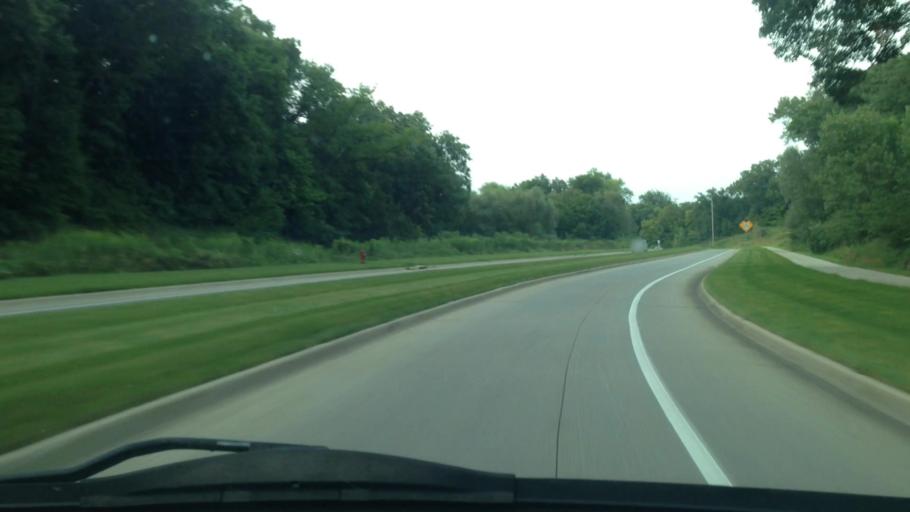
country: US
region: Iowa
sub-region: Johnson County
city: Coralville
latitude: 41.6739
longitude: -91.6015
